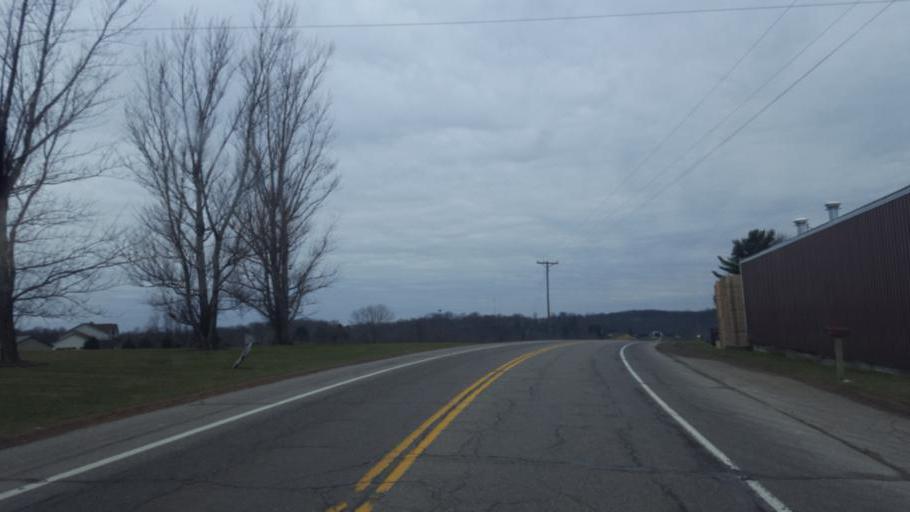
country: US
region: Ohio
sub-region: Tuscarawas County
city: Sugarcreek
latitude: 40.6049
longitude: -81.7219
